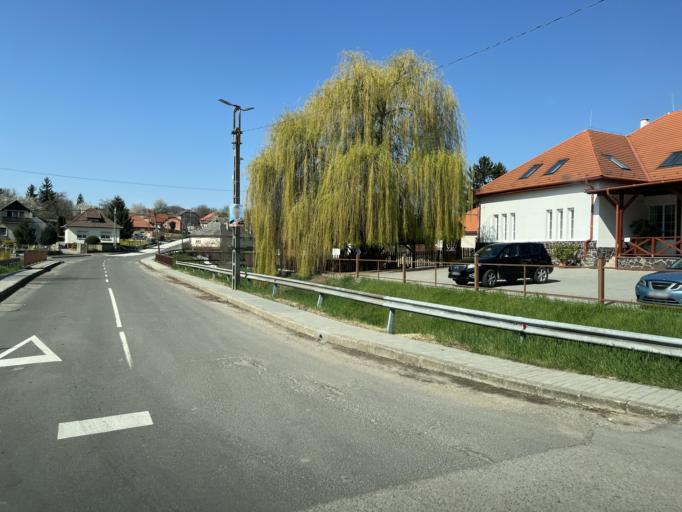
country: HU
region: Pest
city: Orbottyan
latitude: 47.7411
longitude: 19.3149
